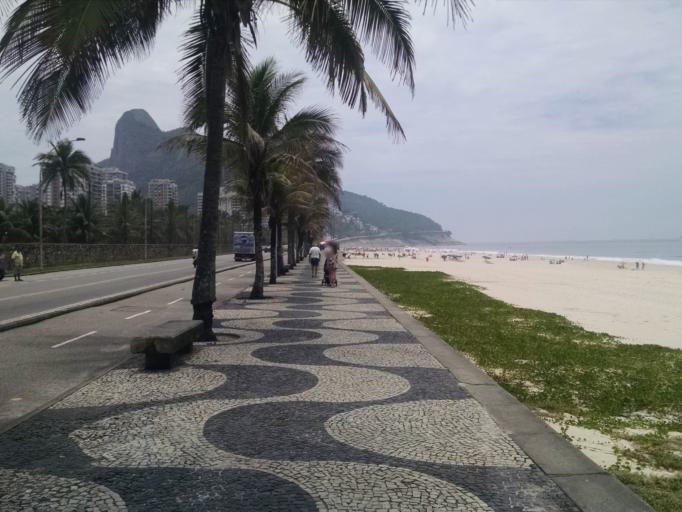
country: BR
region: Rio de Janeiro
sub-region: Rio De Janeiro
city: Rio de Janeiro
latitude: -22.9995
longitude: -43.2646
